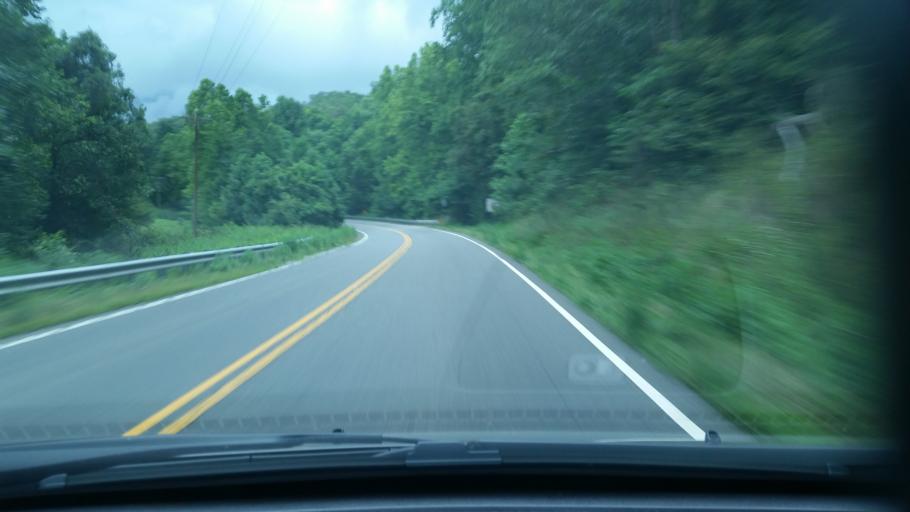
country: US
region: Virginia
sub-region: Nelson County
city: Nellysford
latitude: 37.8734
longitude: -78.8201
